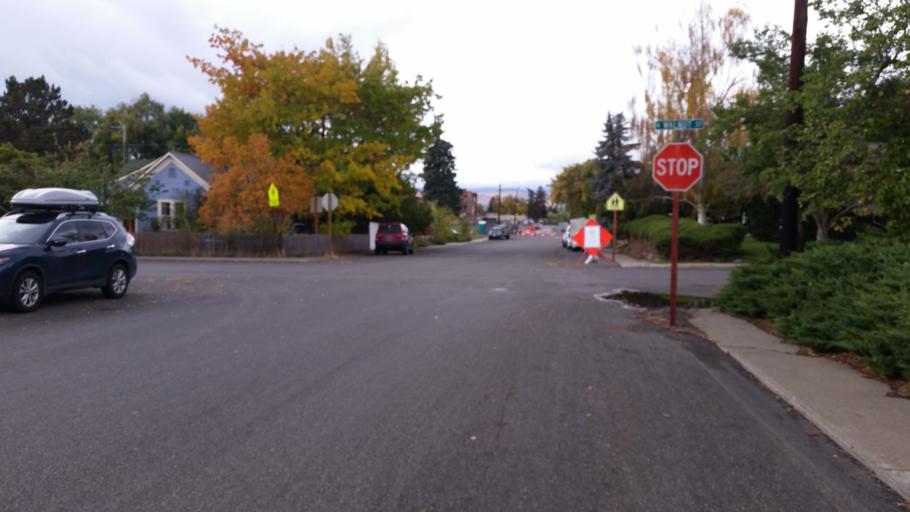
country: US
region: Washington
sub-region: Kittitas County
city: Ellensburg
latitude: 46.9926
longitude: -120.5387
